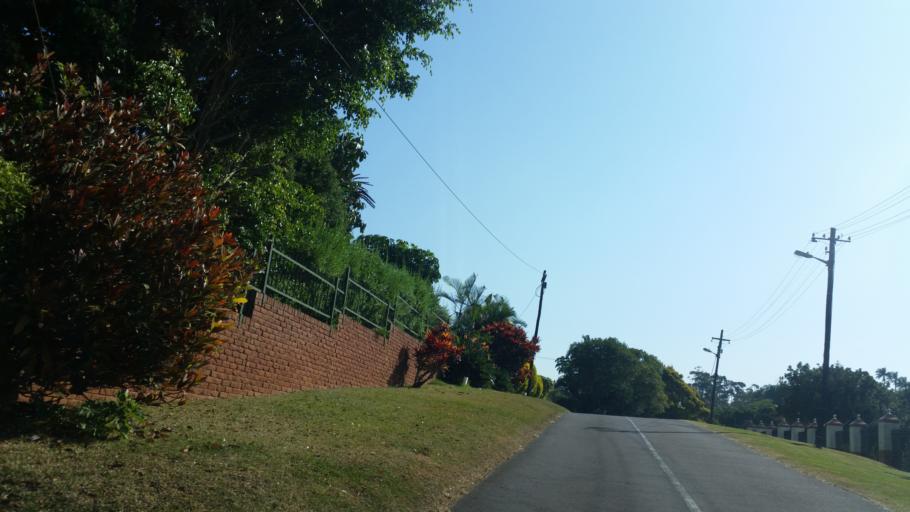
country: ZA
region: KwaZulu-Natal
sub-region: eThekwini Metropolitan Municipality
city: Berea
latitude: -29.8501
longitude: 30.8994
